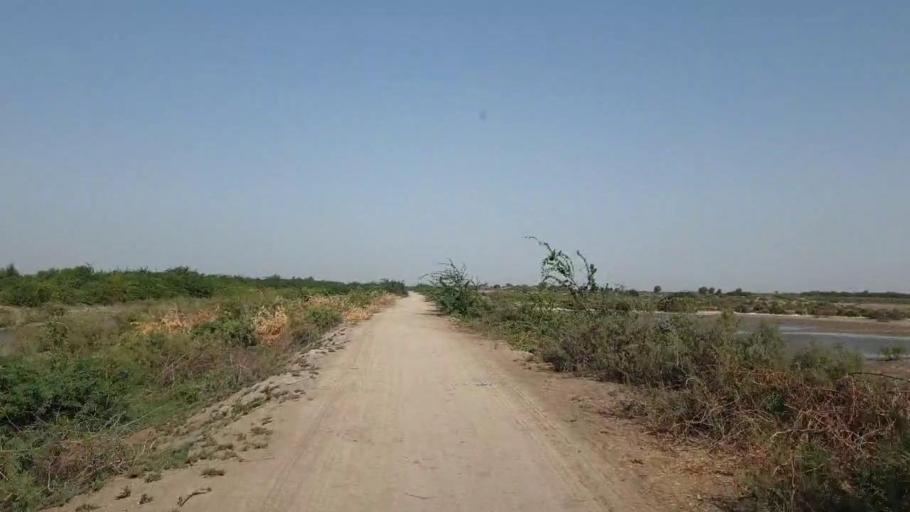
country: PK
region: Sindh
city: Tando Bago
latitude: 24.6435
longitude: 69.0721
